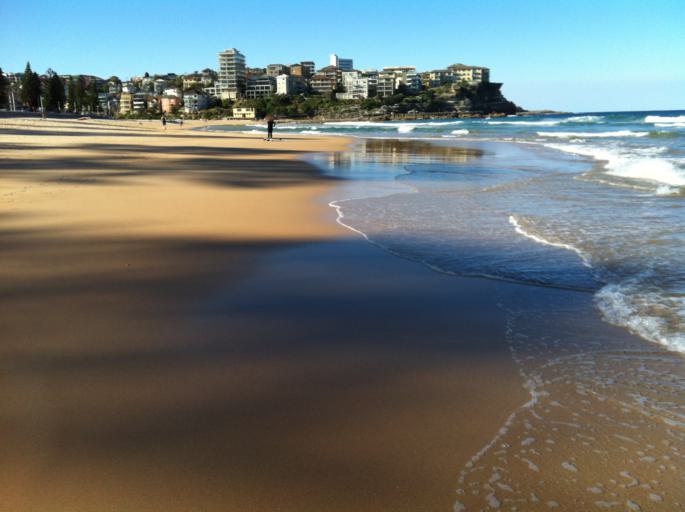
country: AU
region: New South Wales
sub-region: Manly Vale
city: Manly
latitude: -33.7893
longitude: 151.2880
